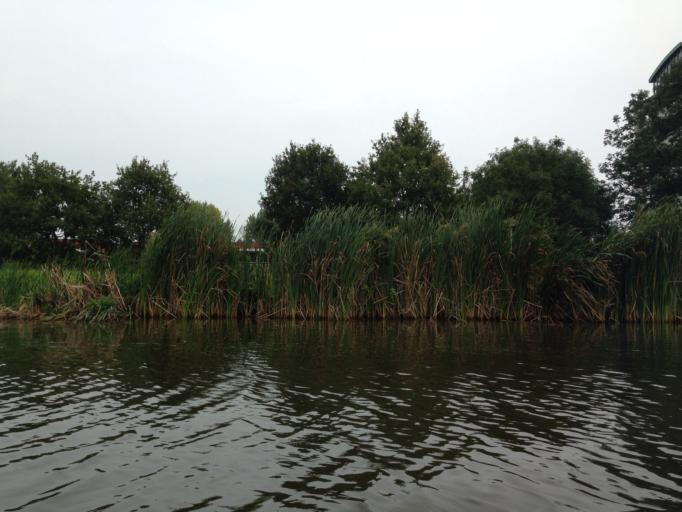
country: NL
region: South Holland
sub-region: Gemeente Vlaardingen
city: Vlaardingen
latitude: 51.9321
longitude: 4.3343
